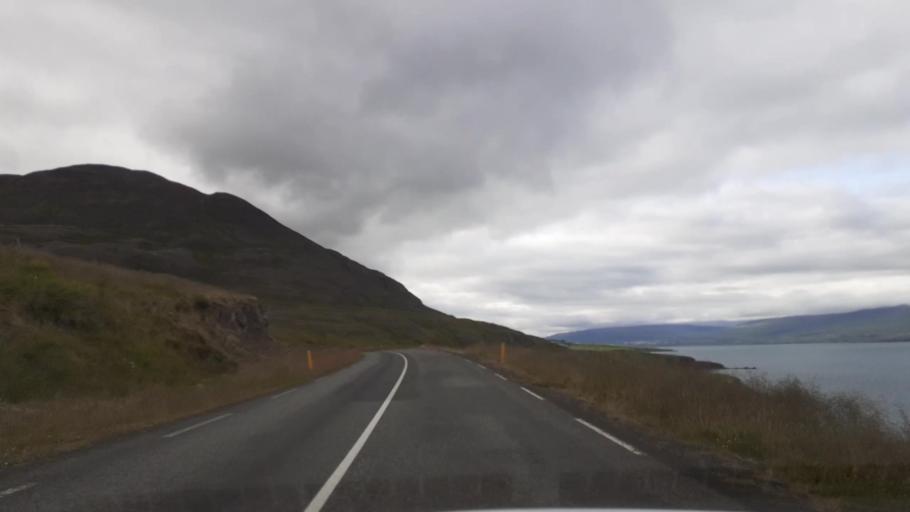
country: IS
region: Northeast
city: Akureyri
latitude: 65.8212
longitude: -18.0503
